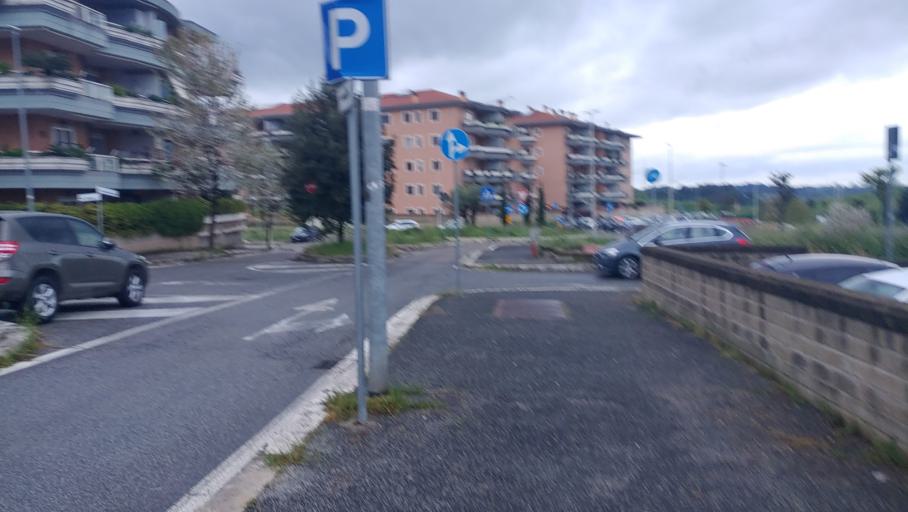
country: IT
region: Latium
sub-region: Citta metropolitana di Roma Capitale
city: La Massimina-Casal Lumbroso
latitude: 41.9080
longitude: 12.3869
